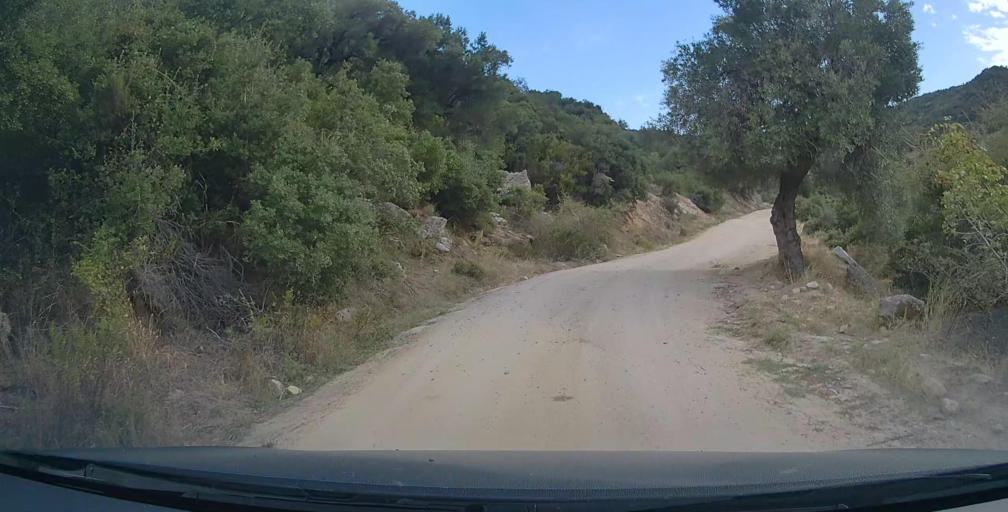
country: GR
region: Central Macedonia
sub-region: Nomos Chalkidikis
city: Sykia
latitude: 40.0155
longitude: 23.9388
